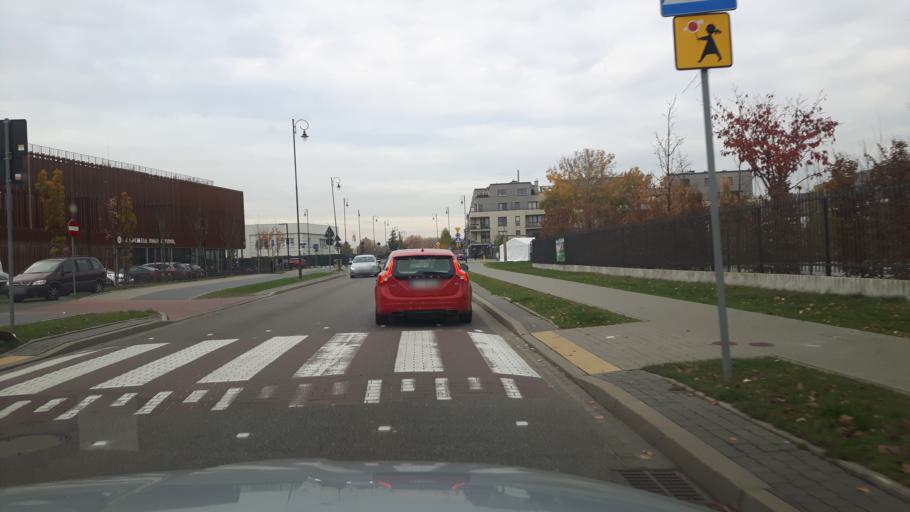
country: PL
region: Masovian Voivodeship
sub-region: Warszawa
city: Ursynow
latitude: 52.1576
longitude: 21.0683
